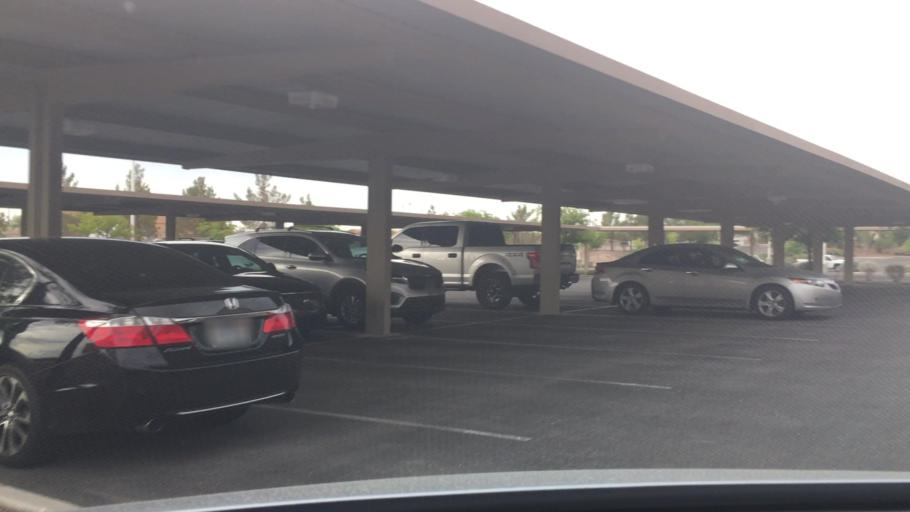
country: US
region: Nevada
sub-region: Clark County
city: Summerlin South
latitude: 36.0719
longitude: -115.2939
